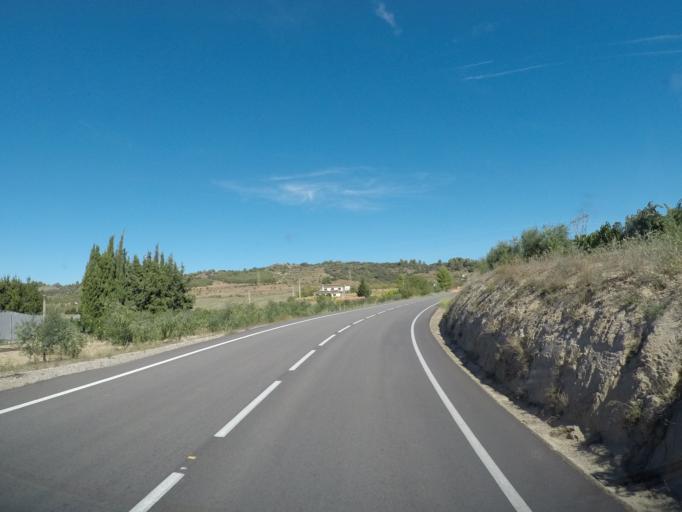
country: ES
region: Catalonia
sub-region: Provincia de Tarragona
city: Falset
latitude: 41.1569
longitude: 0.8147
